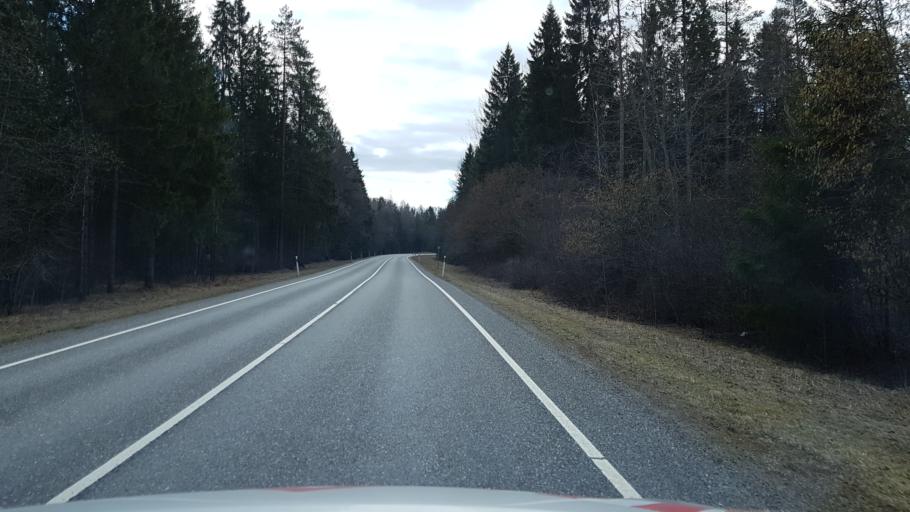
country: EE
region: Laeaene-Virumaa
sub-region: Vaeike-Maarja vald
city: Vaike-Maarja
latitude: 59.0687
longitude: 26.2379
